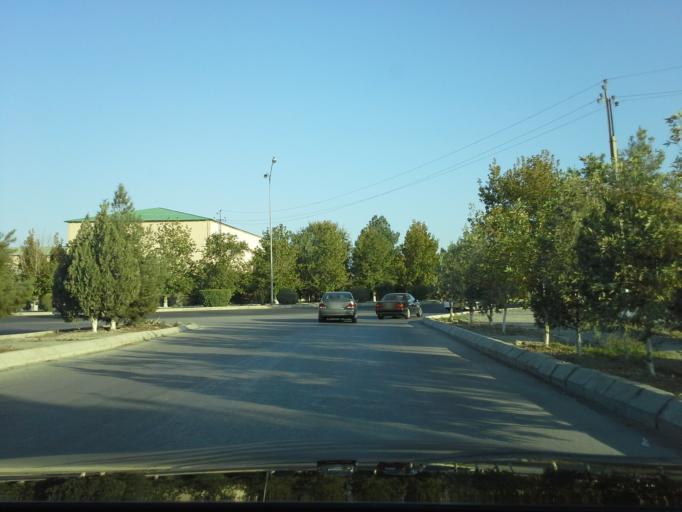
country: TM
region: Ahal
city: Abadan
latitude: 38.0455
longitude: 58.1857
